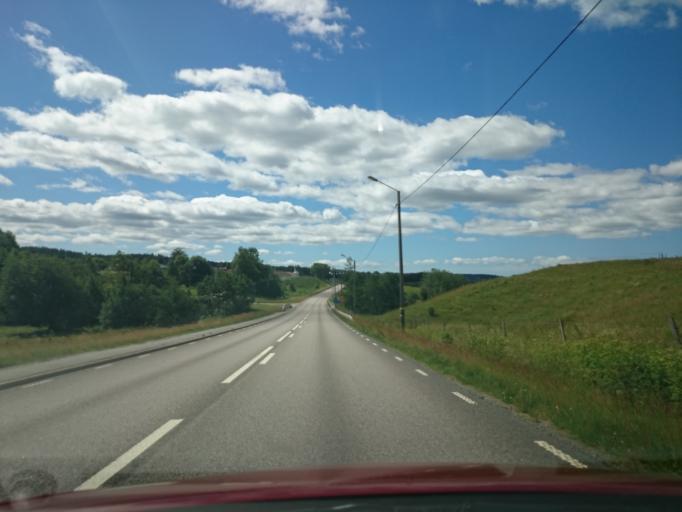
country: SE
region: Vaestra Goetaland
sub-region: Partille Kommun
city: Partille
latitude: 57.8094
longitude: 12.1720
